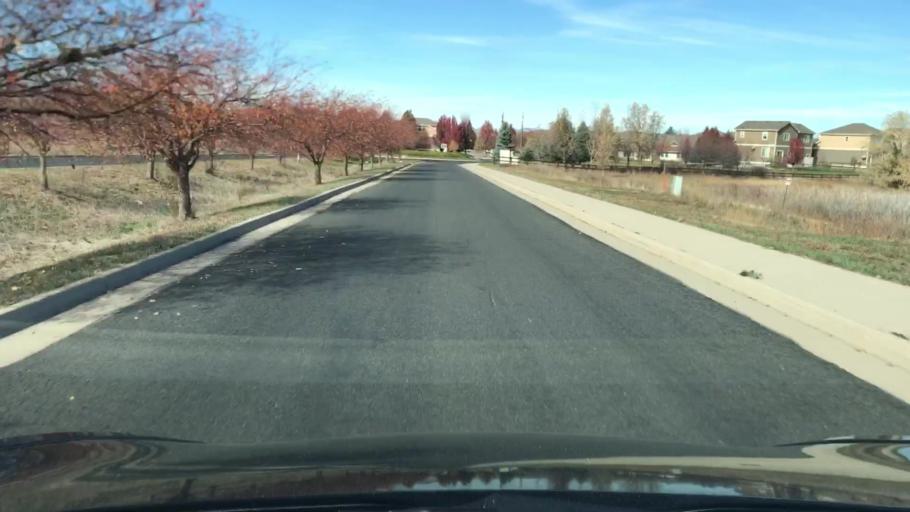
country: US
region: Colorado
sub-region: Larimer County
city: Fort Collins
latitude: 40.5893
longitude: -105.0388
